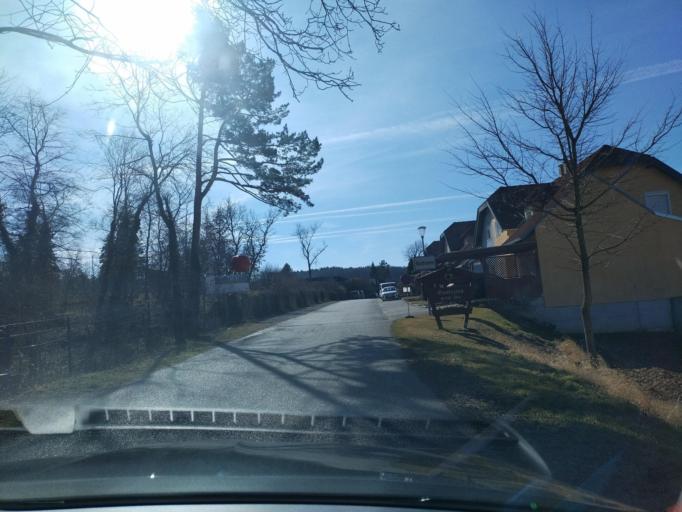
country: AT
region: Lower Austria
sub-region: Politischer Bezirk Neunkirchen
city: Breitenau
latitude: 47.7203
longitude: 16.1568
